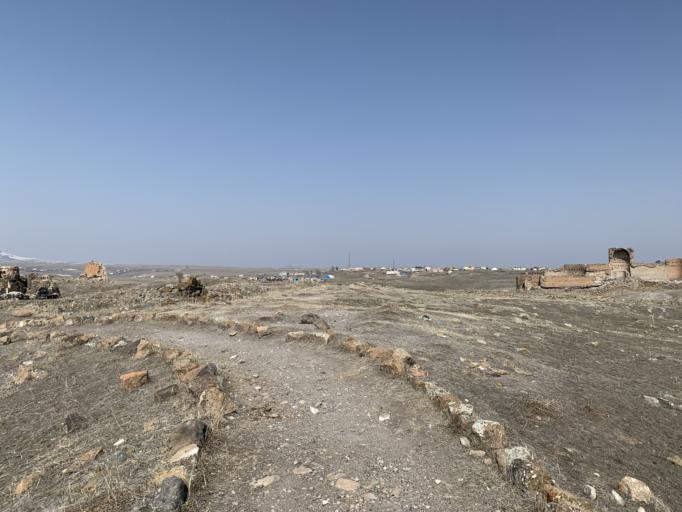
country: TR
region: Kars
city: Basgedikler
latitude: 40.5098
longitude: 43.5696
